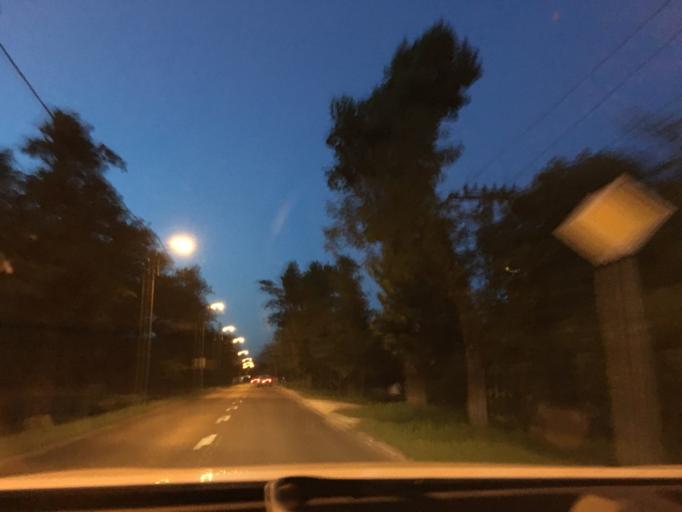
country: HU
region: Budapest
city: Budapest XVII. keruelet
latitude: 47.4718
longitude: 19.2525
